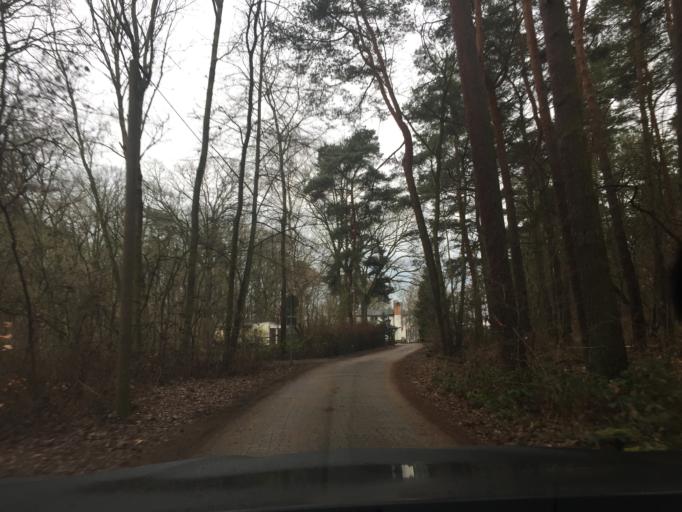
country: DE
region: Berlin
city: Kladow
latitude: 52.4534
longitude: 13.1071
